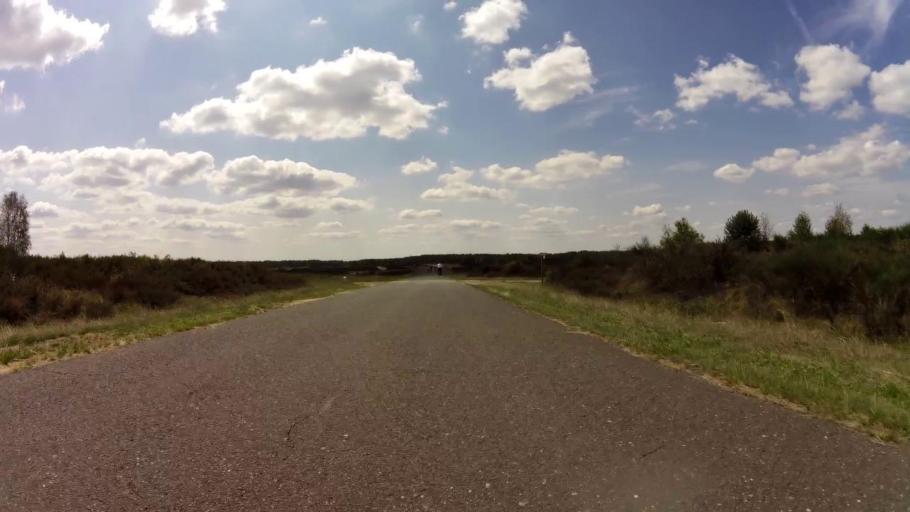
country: PL
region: West Pomeranian Voivodeship
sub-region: Powiat drawski
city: Drawsko Pomorskie
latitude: 53.4179
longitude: 15.7407
